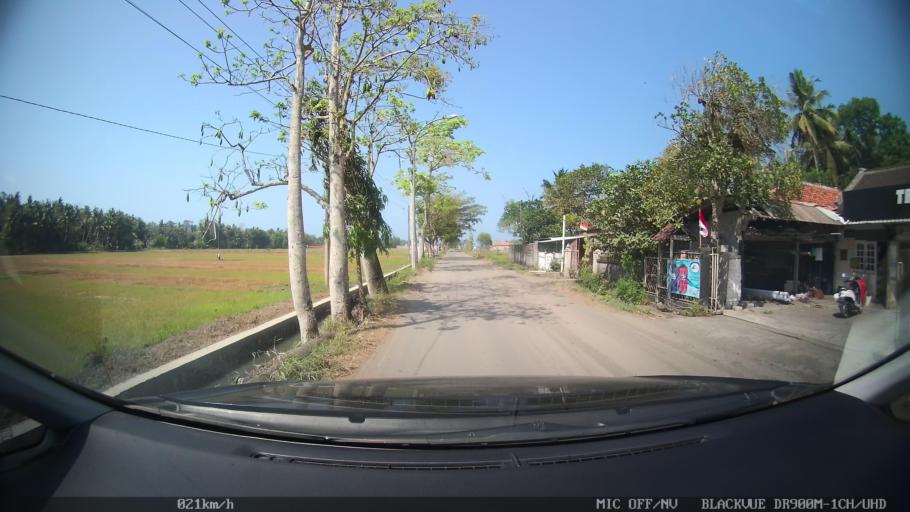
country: ID
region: Daerah Istimewa Yogyakarta
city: Srandakan
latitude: -7.9532
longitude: 110.2182
